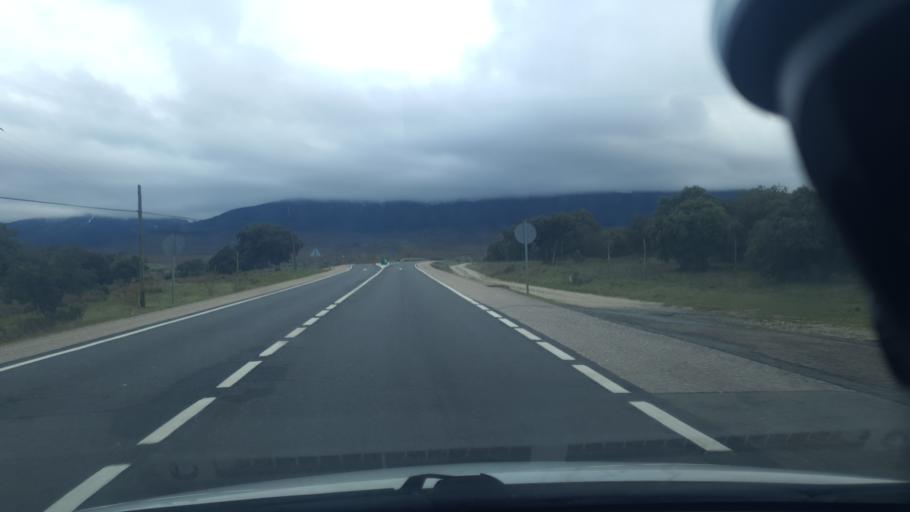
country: ES
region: Castille and Leon
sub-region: Provincia de Segovia
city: Cerezo de Abajo
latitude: 41.2118
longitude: -3.5837
